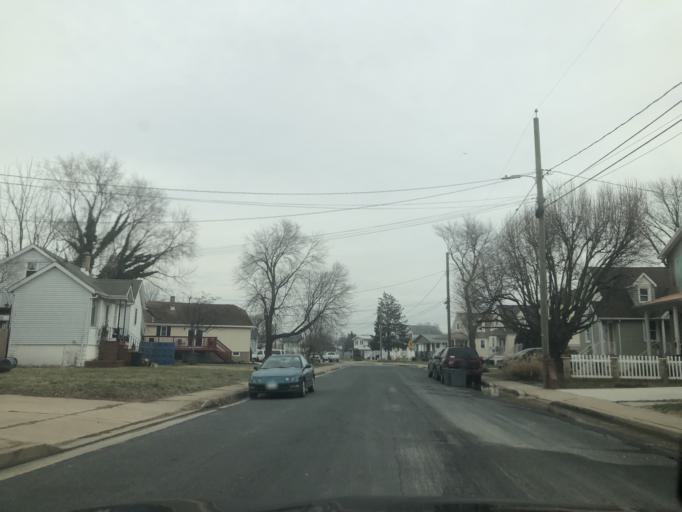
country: US
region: Maryland
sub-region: Baltimore County
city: Edgemere
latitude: 39.2599
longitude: -76.4819
